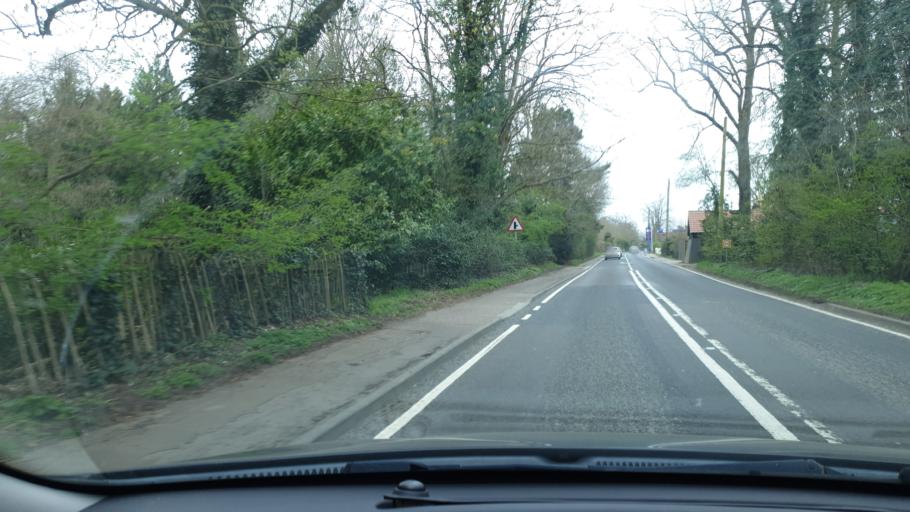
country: GB
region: England
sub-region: Essex
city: Great Horkesley
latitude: 51.9319
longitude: 0.8764
